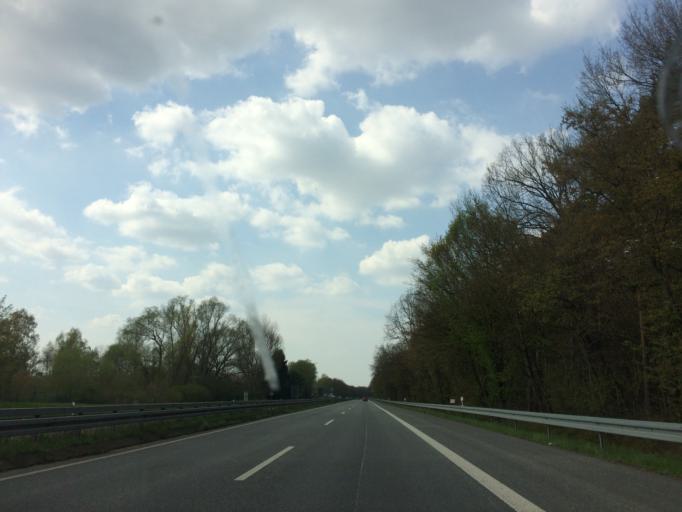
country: DE
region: Hesse
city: Obertshausen
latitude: 50.0862
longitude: 8.8392
